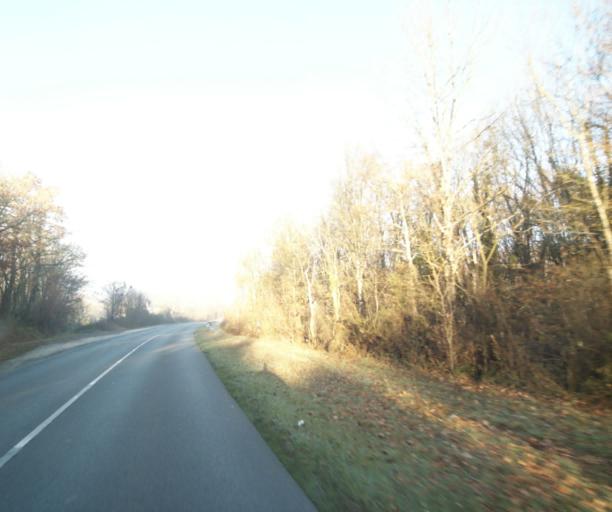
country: FR
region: Poitou-Charentes
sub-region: Departement de la Charente-Maritime
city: Bussac-sur-Charente
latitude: 45.7753
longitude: -0.6232
